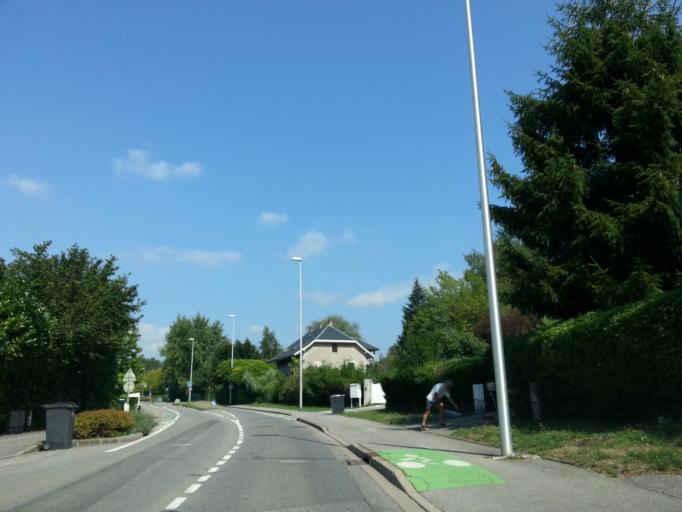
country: FR
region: Rhone-Alpes
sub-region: Departement de la Haute-Savoie
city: Annecy-le-Vieux
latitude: 45.9110
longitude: 6.1569
